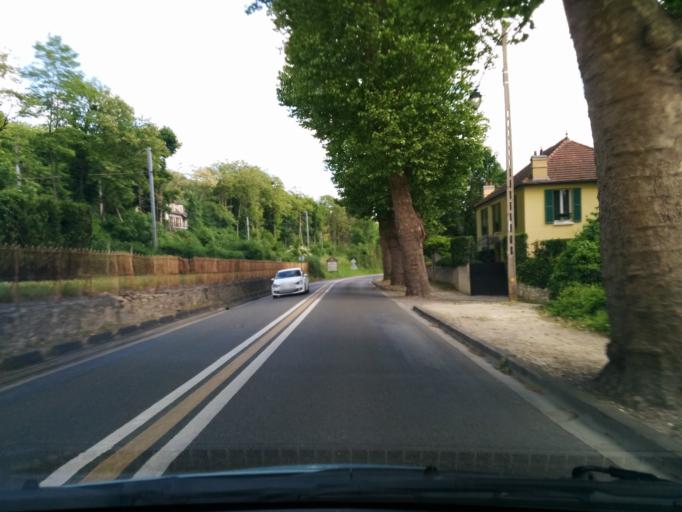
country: FR
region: Ile-de-France
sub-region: Departement des Yvelines
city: Maule
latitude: 48.9066
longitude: 1.8611
